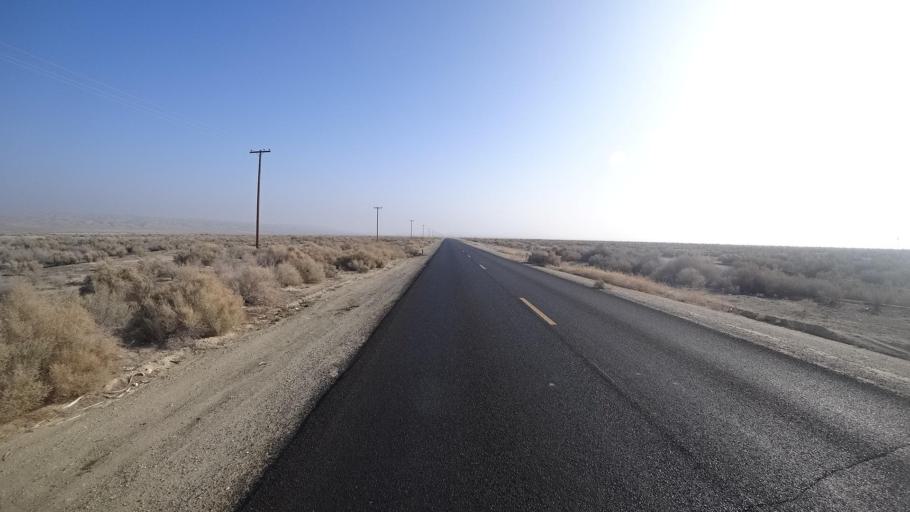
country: US
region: California
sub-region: Kern County
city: Taft Heights
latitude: 35.1805
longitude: -119.5120
